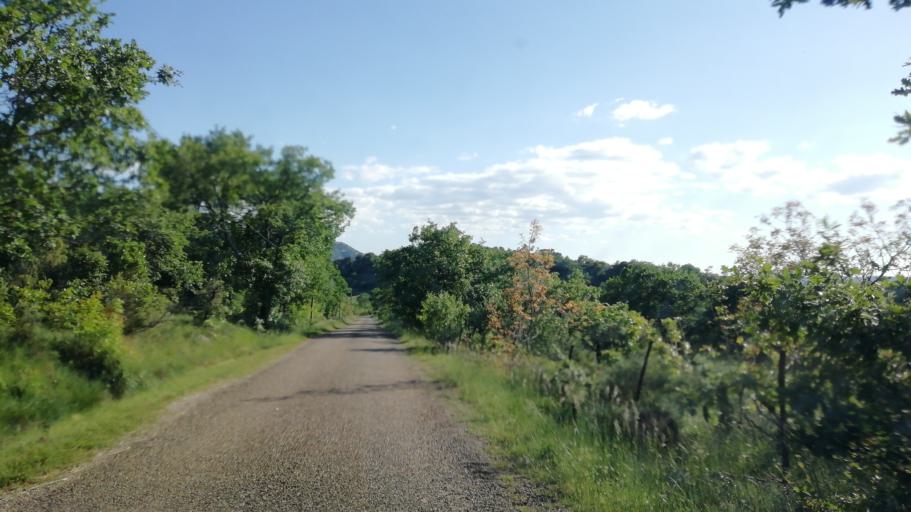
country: FR
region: Languedoc-Roussillon
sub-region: Departement de l'Herault
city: Saint-Mathieu-de-Treviers
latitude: 43.8108
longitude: 3.8118
